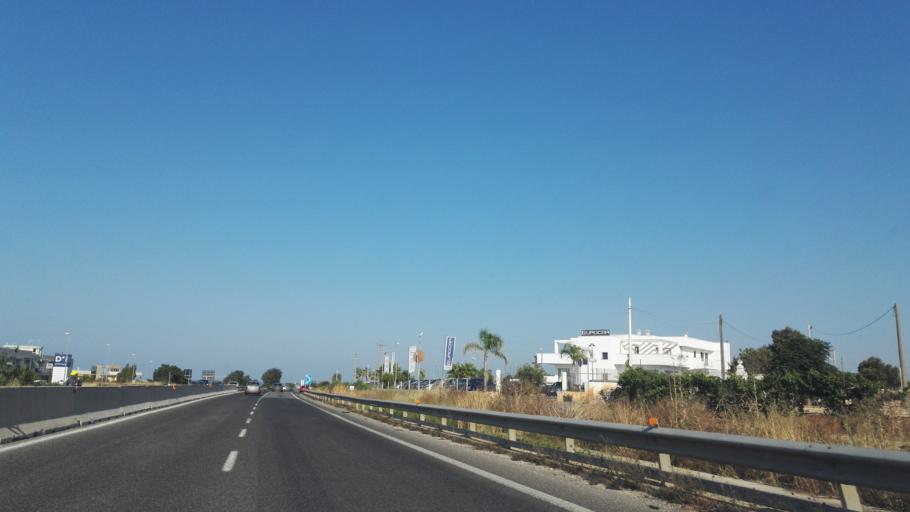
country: IT
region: Apulia
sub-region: Provincia di Bari
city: Polignano a Mare
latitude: 40.9874
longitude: 17.2172
